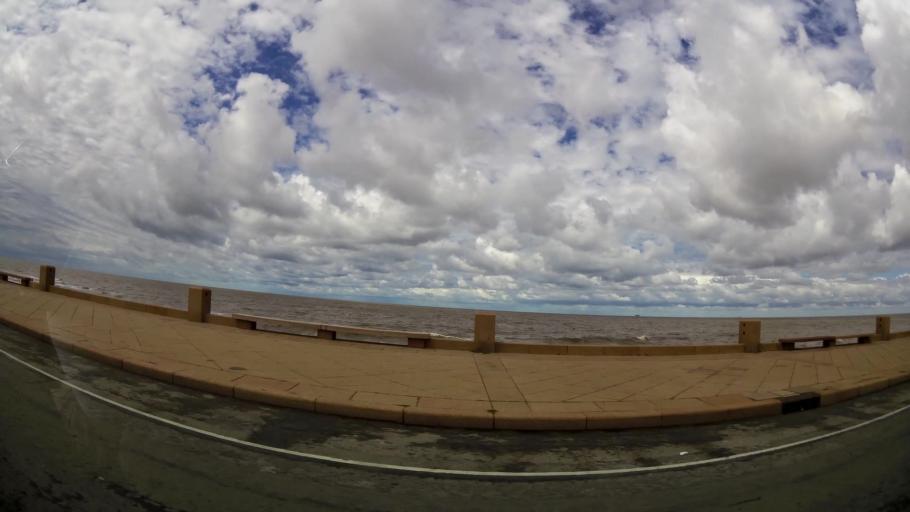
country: UY
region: Montevideo
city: Montevideo
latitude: -34.9155
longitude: -56.1870
